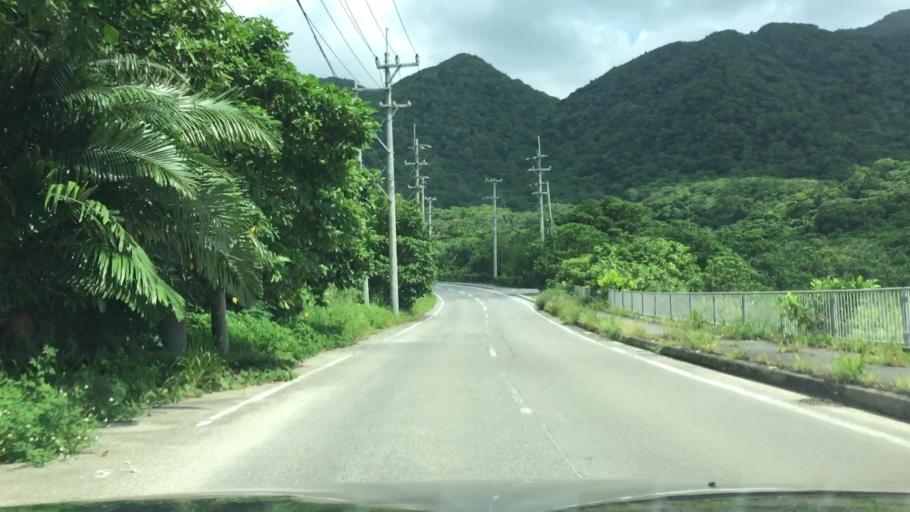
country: JP
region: Okinawa
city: Ishigaki
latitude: 24.4533
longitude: 124.2113
